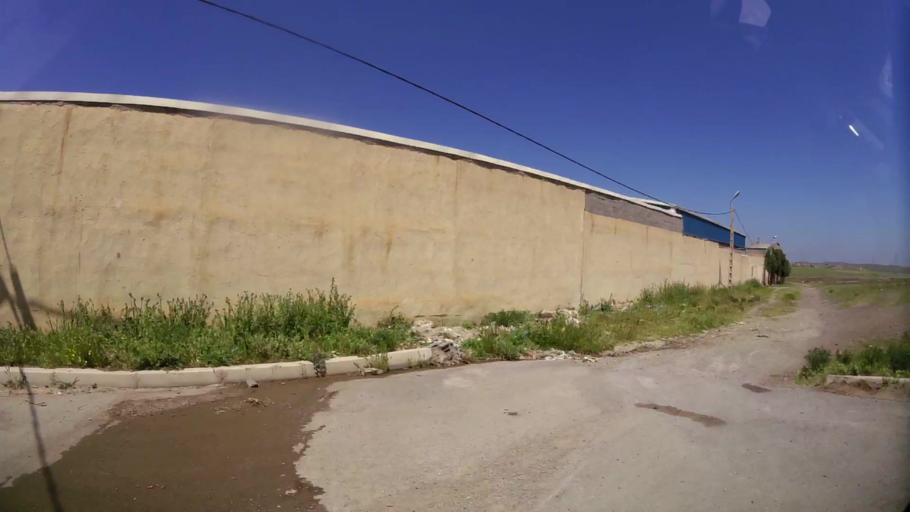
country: MA
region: Oriental
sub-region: Oujda-Angad
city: Oujda
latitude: 34.6833
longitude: -1.9608
